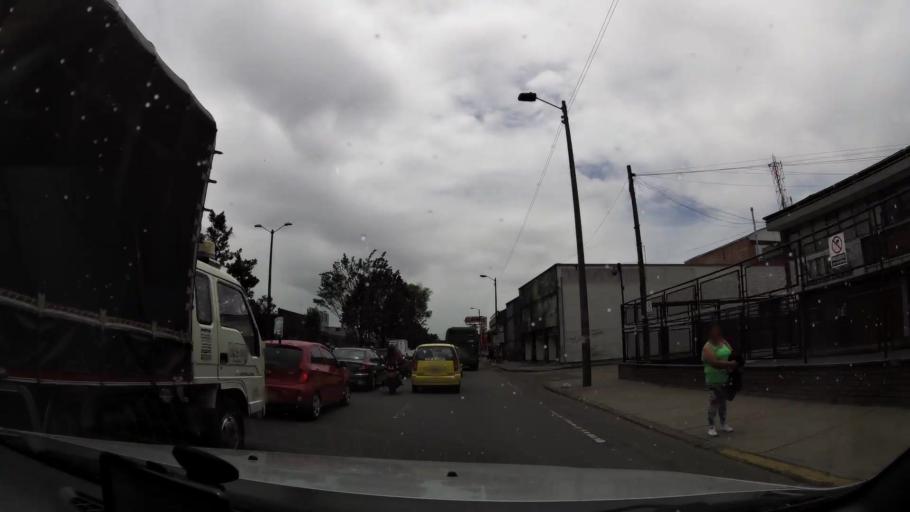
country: CO
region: Bogota D.C.
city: Bogota
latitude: 4.6414
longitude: -74.1144
